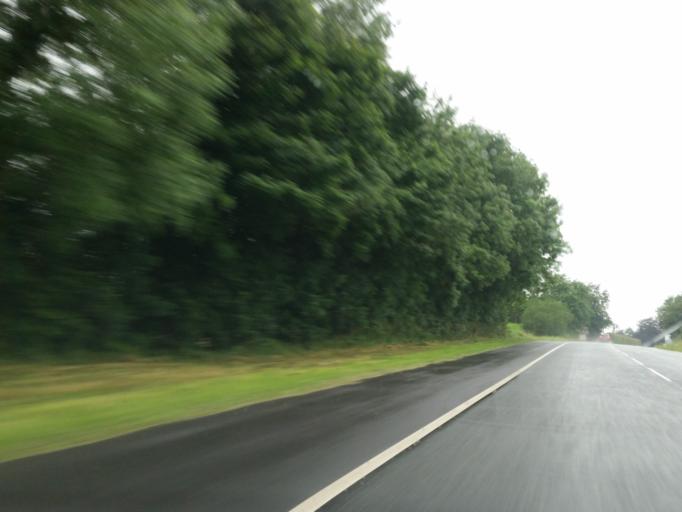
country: GB
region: Northern Ireland
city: Fivemiletown
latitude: 54.3687
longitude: -7.3360
